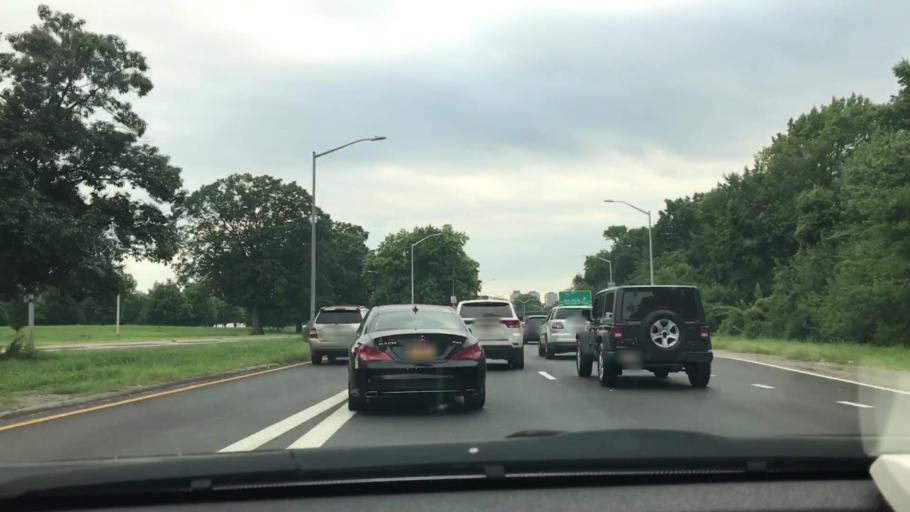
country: US
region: New York
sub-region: Bronx
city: Eastchester
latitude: 40.8574
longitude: -73.8219
